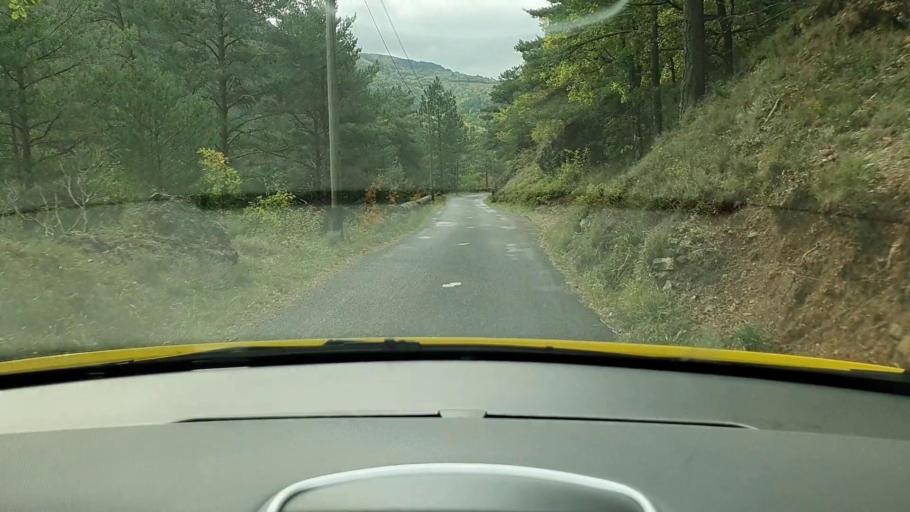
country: FR
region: Languedoc-Roussillon
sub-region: Departement de la Lozere
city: Meyrueis
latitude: 44.0866
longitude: 3.3944
